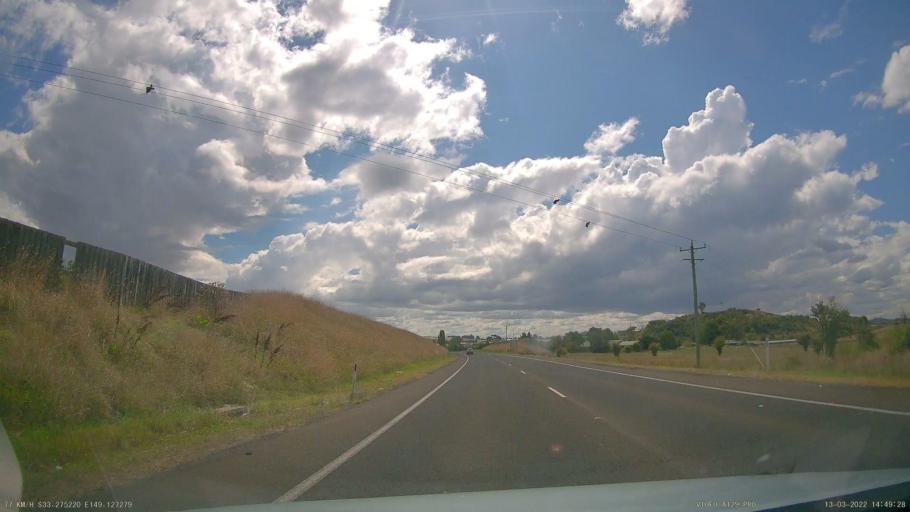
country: AU
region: New South Wales
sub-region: Orange Municipality
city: Orange
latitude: -33.2751
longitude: 149.1273
